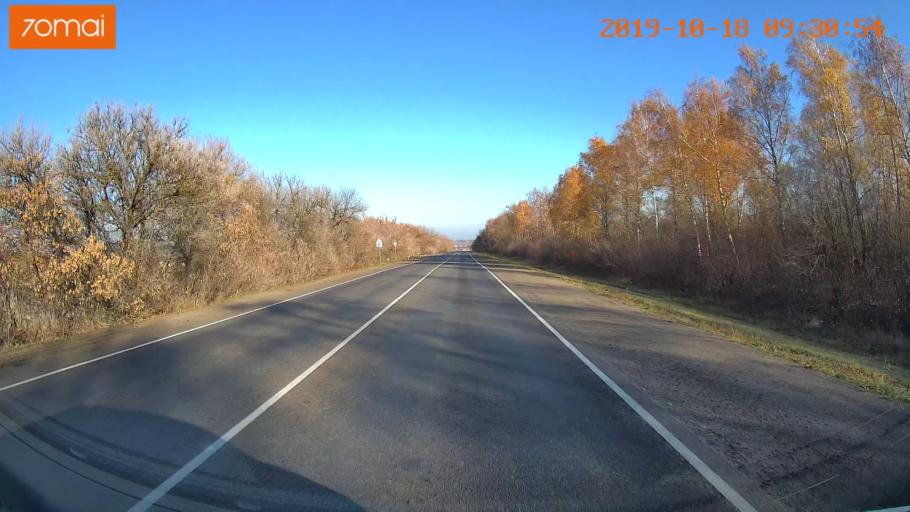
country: RU
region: Tula
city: Yefremov
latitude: 53.1438
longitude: 38.1590
